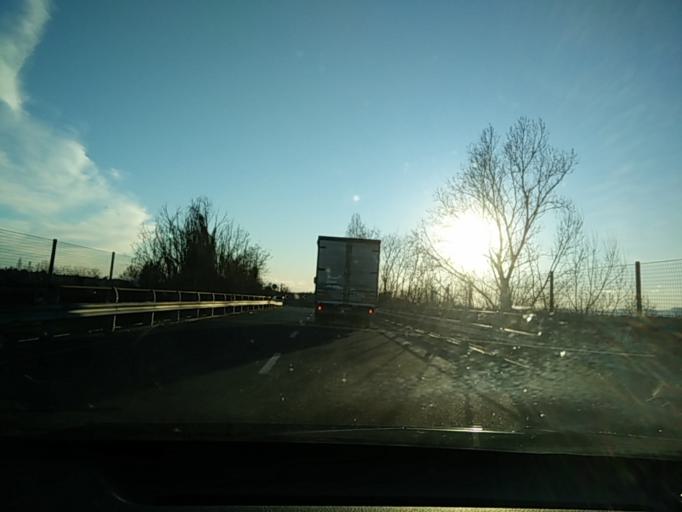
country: IT
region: Friuli Venezia Giulia
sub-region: Provincia di Udine
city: Colugna
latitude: 46.1087
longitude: 13.2035
